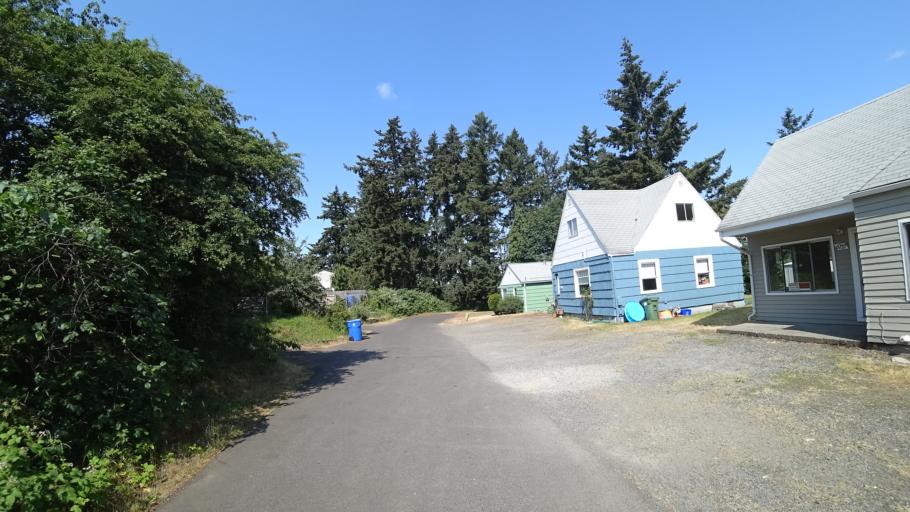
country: US
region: Oregon
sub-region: Multnomah County
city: Lents
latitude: 45.4532
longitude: -122.5941
